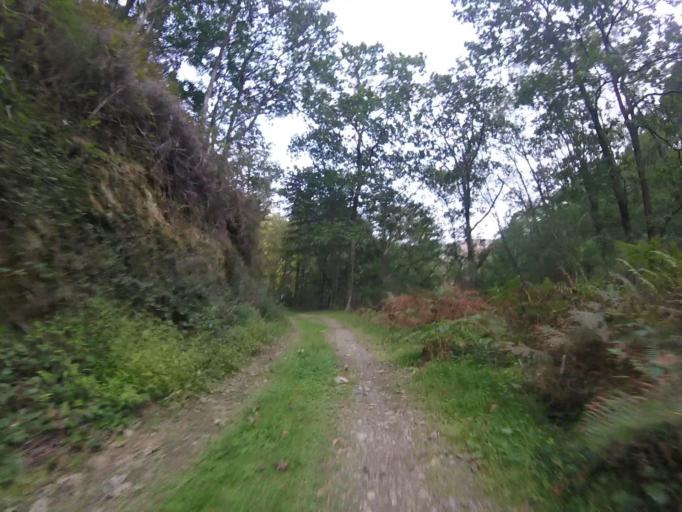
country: ES
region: Navarre
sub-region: Provincia de Navarra
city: Arano
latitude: 43.2510
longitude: -1.8697
